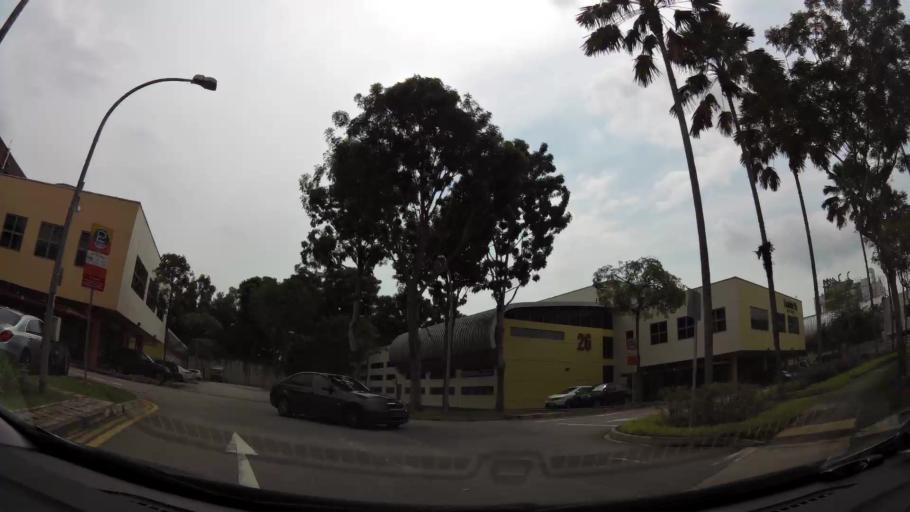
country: SG
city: Singapore
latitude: 1.3527
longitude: 103.9745
